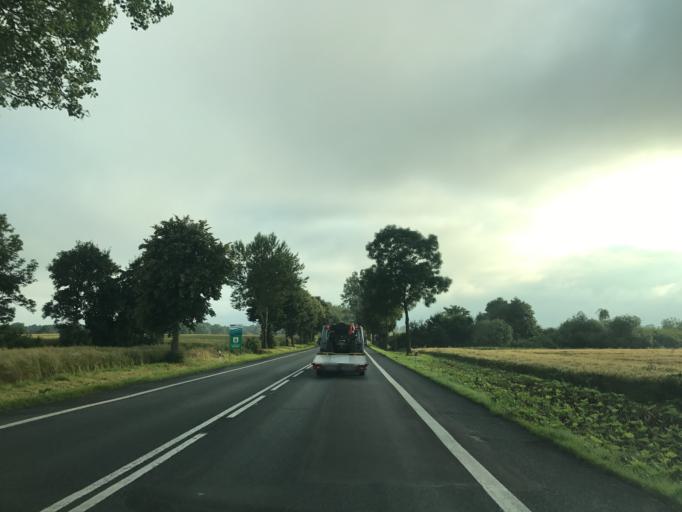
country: PL
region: West Pomeranian Voivodeship
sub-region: Powiat kolobrzeski
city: Goscino
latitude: 53.9888
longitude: 15.7265
